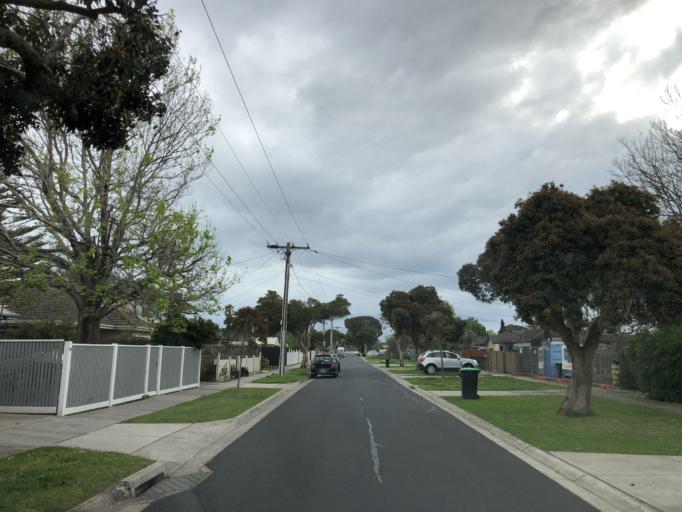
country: AU
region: Victoria
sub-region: Kingston
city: Bonbeach
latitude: -38.0596
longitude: 145.1302
